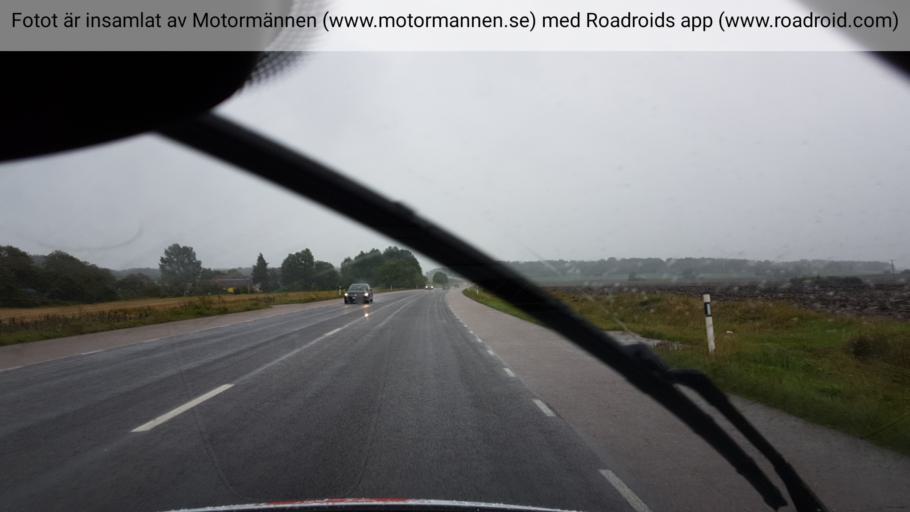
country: SE
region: Halland
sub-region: Laholms Kommun
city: Veinge
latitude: 56.5709
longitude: 13.0218
